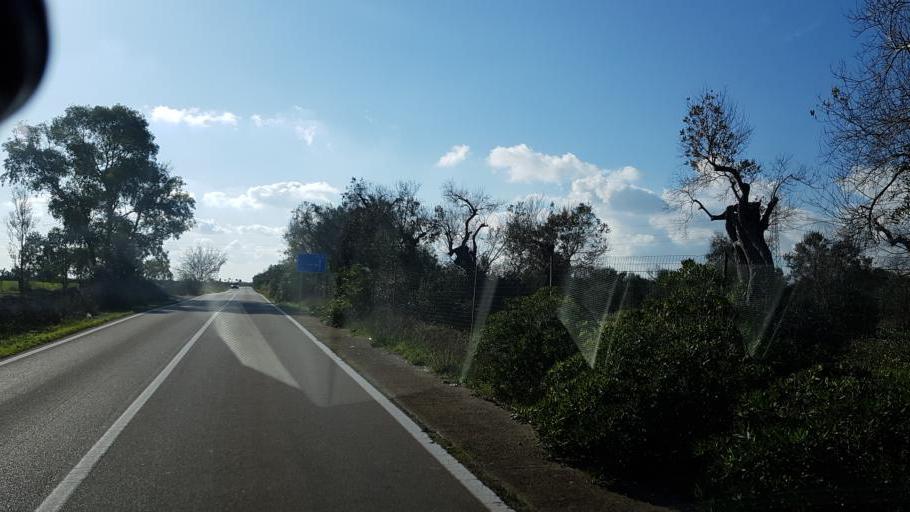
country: IT
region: Apulia
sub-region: Provincia di Lecce
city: Trepuzzi
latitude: 40.4504
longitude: 18.1089
